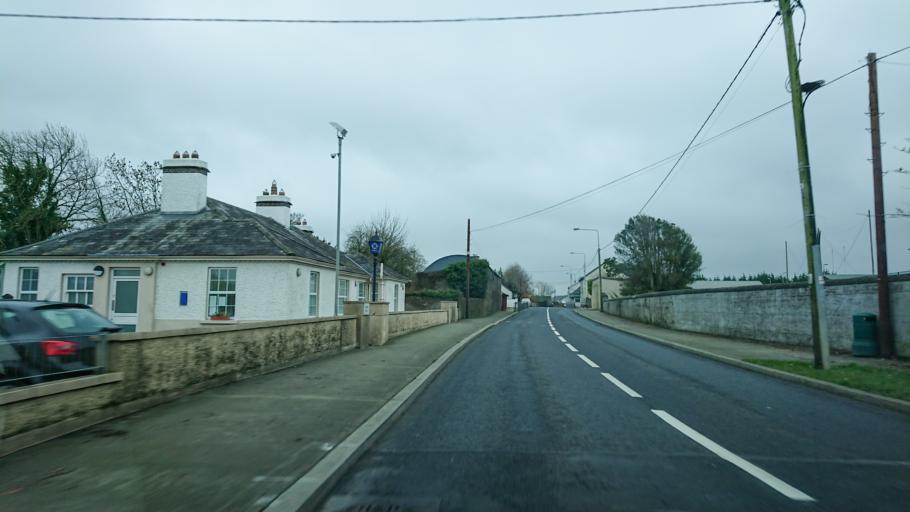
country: IE
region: Leinster
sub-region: Kilkenny
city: Mooncoin
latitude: 52.2949
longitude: -7.2578
